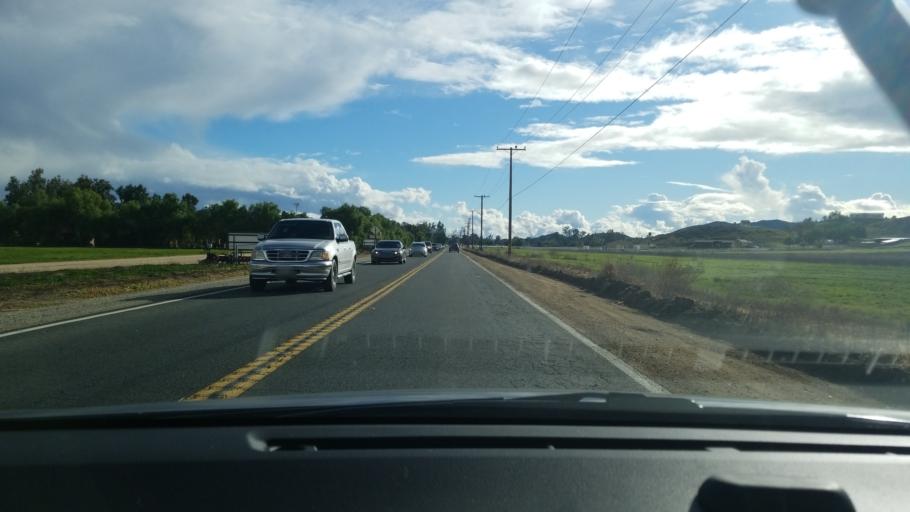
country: US
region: California
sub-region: Riverside County
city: Winchester
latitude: 33.7213
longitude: -117.0764
